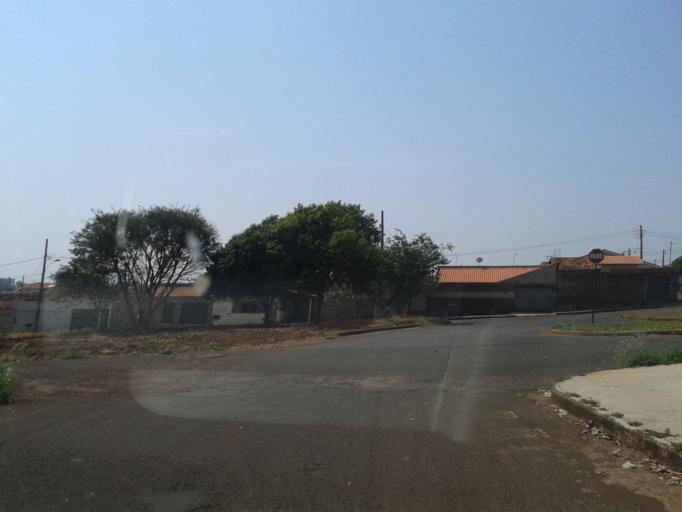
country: BR
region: Minas Gerais
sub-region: Ituiutaba
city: Ituiutaba
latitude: -18.9764
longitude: -49.4883
